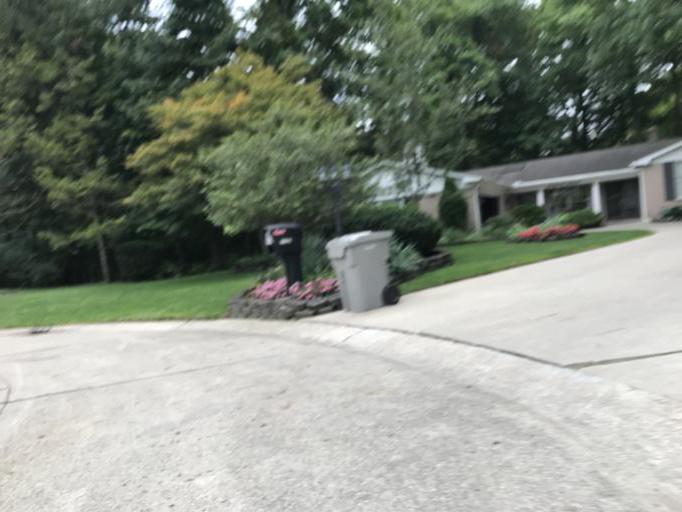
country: US
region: Michigan
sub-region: Oakland County
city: Franklin
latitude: 42.4785
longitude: -83.3258
